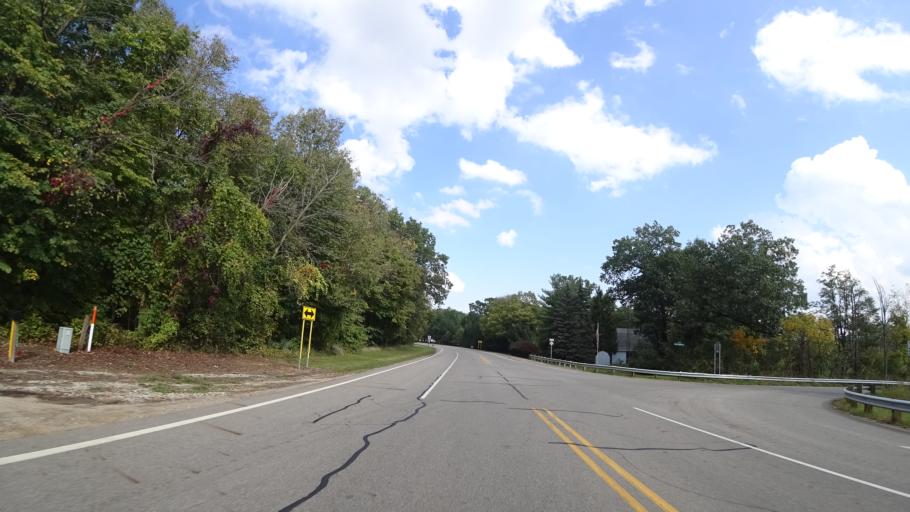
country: US
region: Michigan
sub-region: Saint Joseph County
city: Centreville
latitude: 41.9659
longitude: -85.5701
